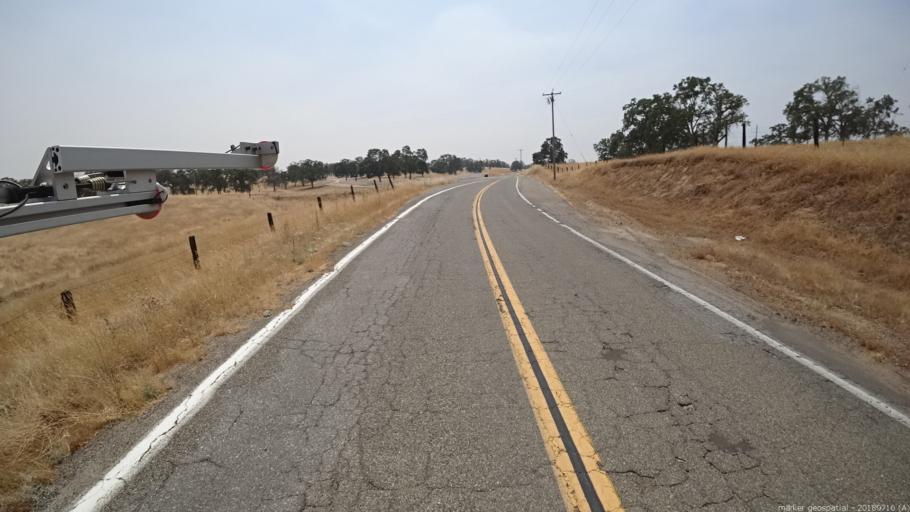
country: US
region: California
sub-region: Madera County
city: Yosemite Lakes
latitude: 37.1925
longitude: -119.9091
